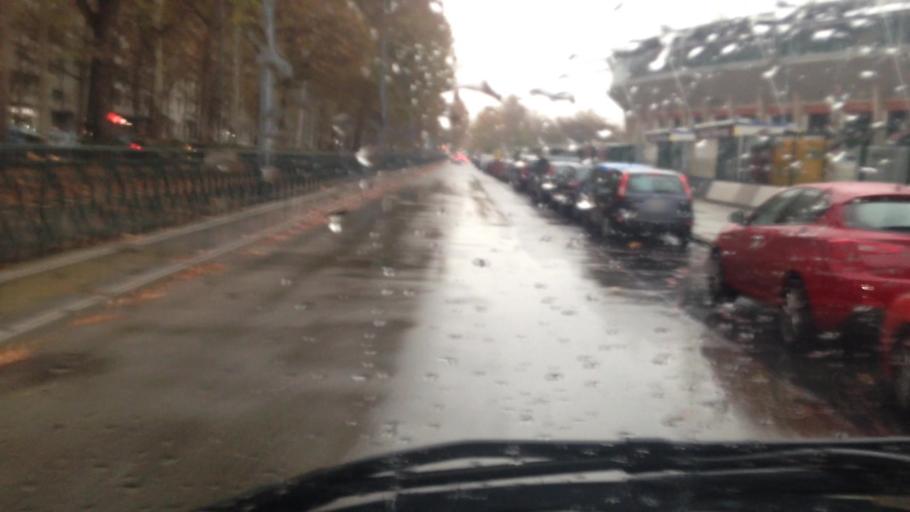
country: IT
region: Piedmont
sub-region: Provincia di Torino
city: Lesna
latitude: 45.0414
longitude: 7.6480
